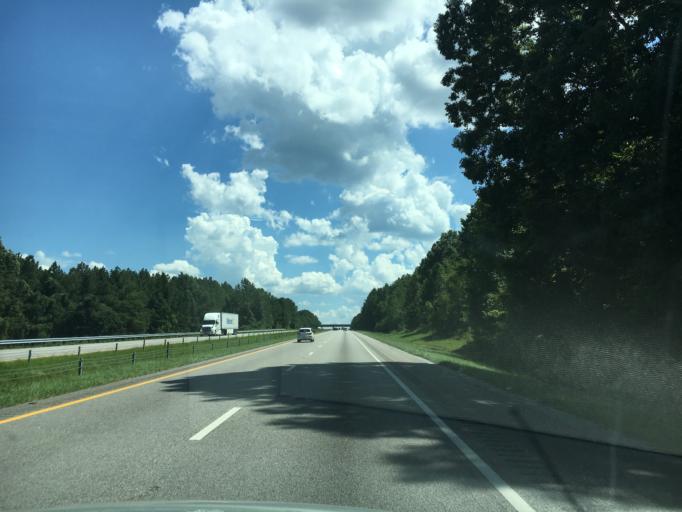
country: US
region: South Carolina
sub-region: Laurens County
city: Clinton
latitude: 34.5681
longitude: -81.8921
